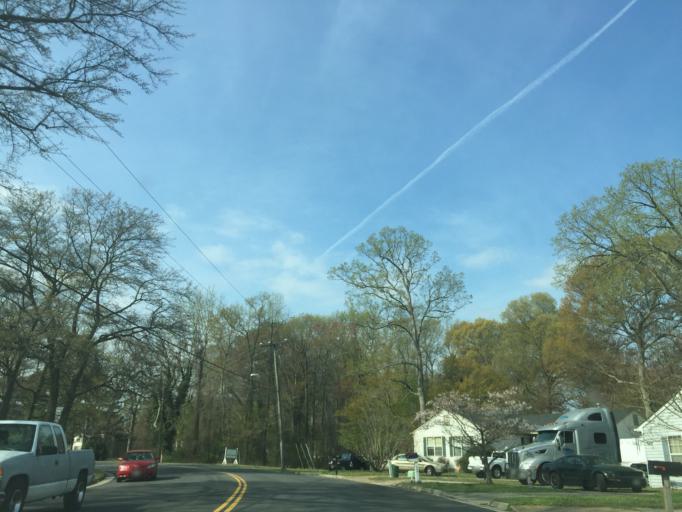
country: US
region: Virginia
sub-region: City of Newport News
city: Newport News
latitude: 37.0759
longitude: -76.4564
